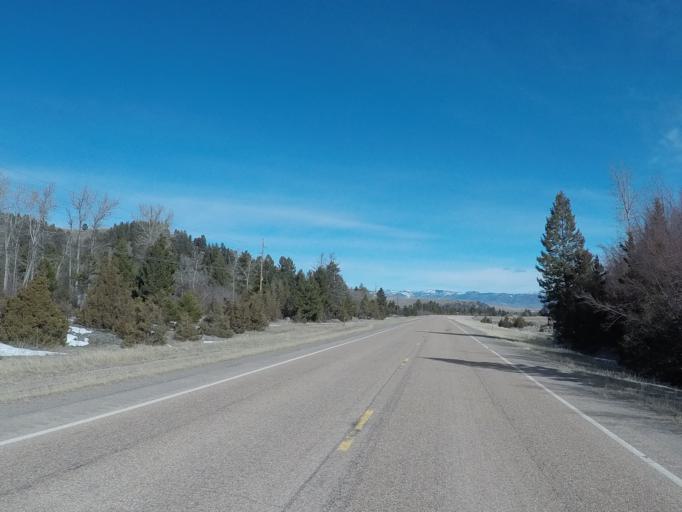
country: US
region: Montana
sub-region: Granite County
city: Philipsburg
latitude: 46.4756
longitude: -113.2346
